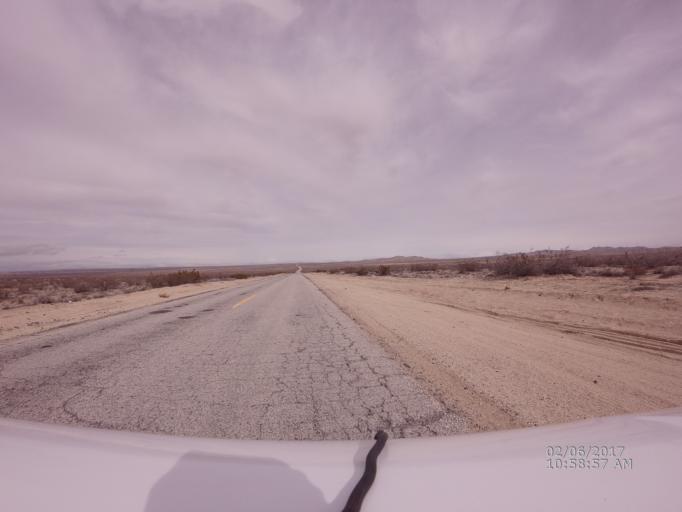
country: US
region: California
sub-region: Los Angeles County
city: Lake Los Angeles
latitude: 34.6340
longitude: -117.7027
